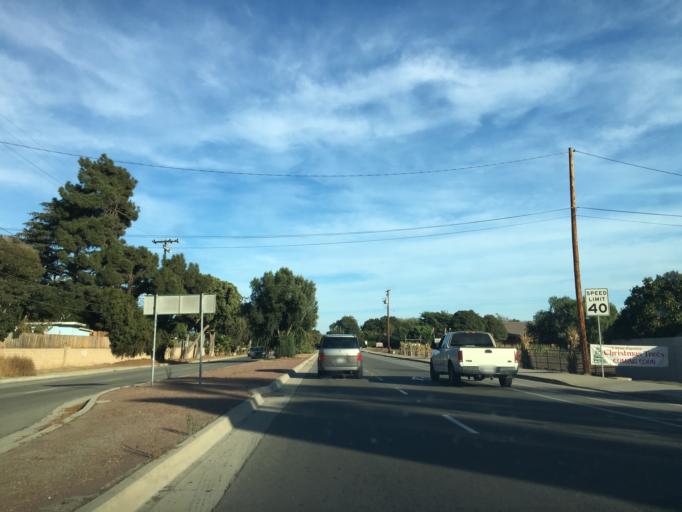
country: US
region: California
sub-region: Santa Barbara County
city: Goleta
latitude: 34.4348
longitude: -119.8017
